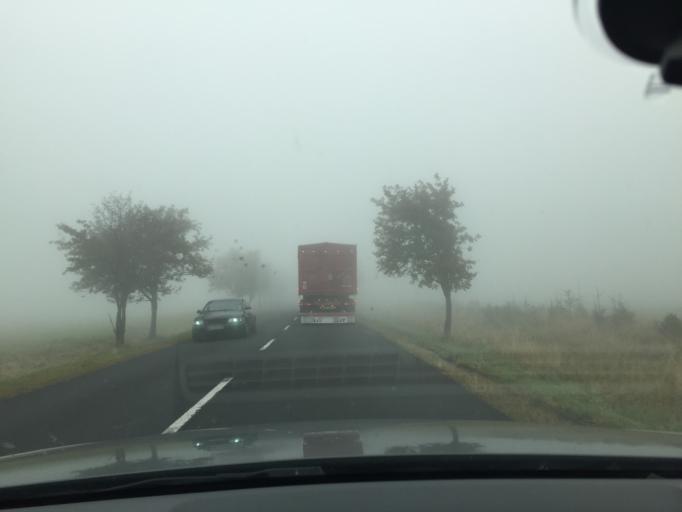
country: CZ
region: Ustecky
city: Libouchec
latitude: 50.7760
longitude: 13.9801
